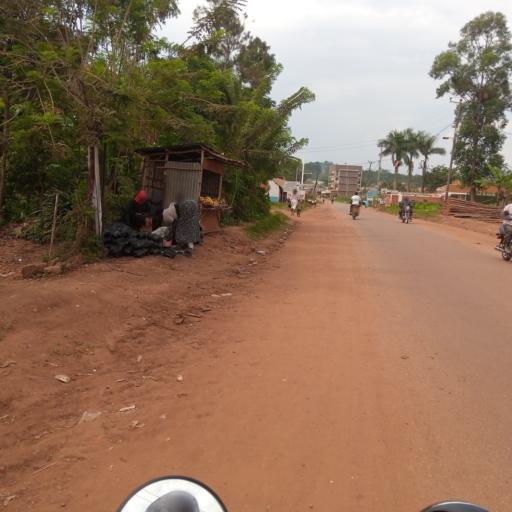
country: UG
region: Eastern Region
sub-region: Mbale District
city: Mbale
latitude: 1.0863
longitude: 34.1819
